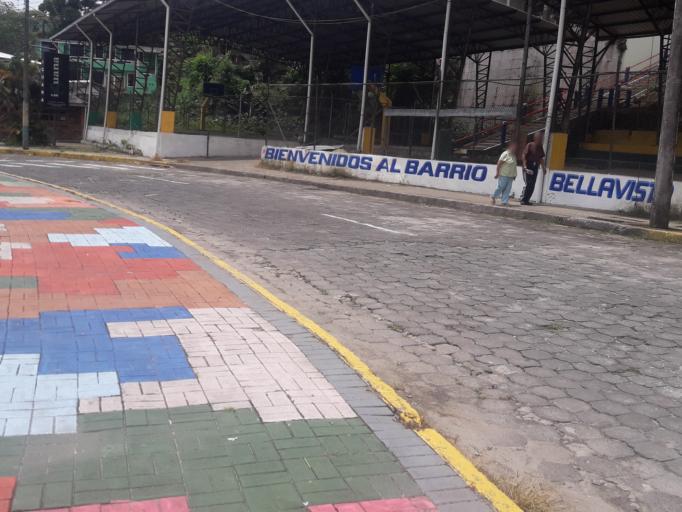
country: EC
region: Napo
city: Tena
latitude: -0.9938
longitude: -77.8121
